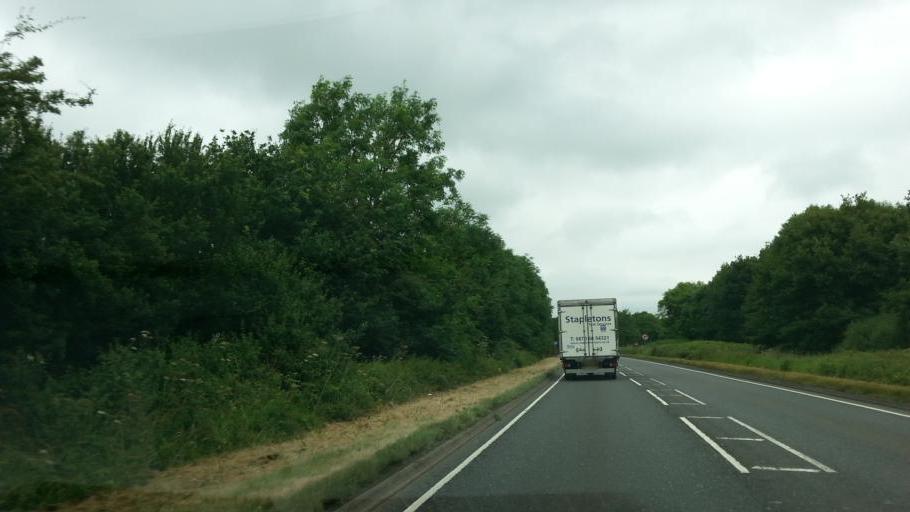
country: GB
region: England
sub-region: Northamptonshire
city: Broughton
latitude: 52.3234
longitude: -0.7946
